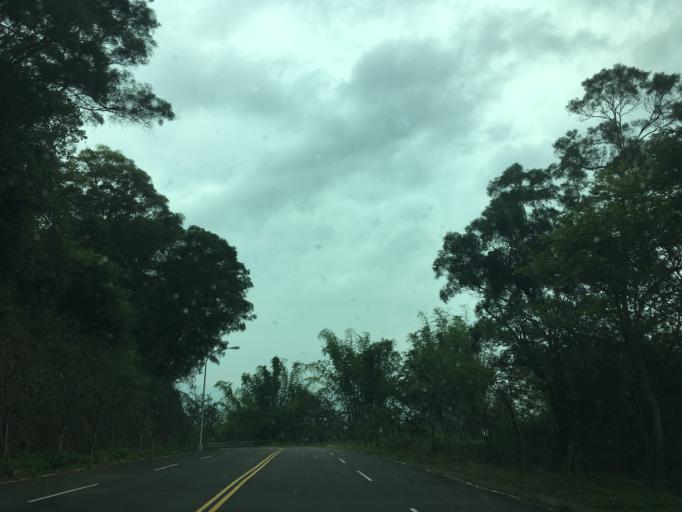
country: TW
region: Taiwan
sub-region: Taichung City
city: Taichung
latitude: 24.0628
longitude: 120.7250
